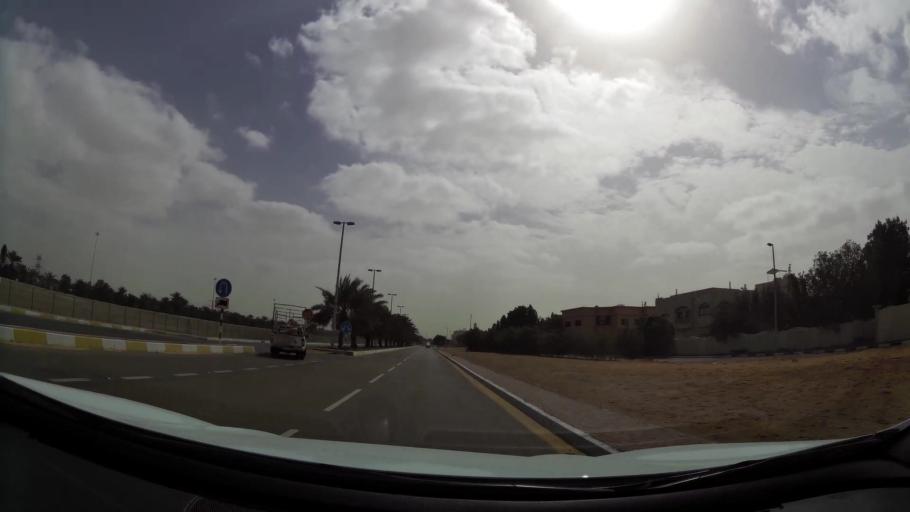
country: AE
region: Abu Dhabi
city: Abu Dhabi
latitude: 24.4089
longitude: 54.5132
